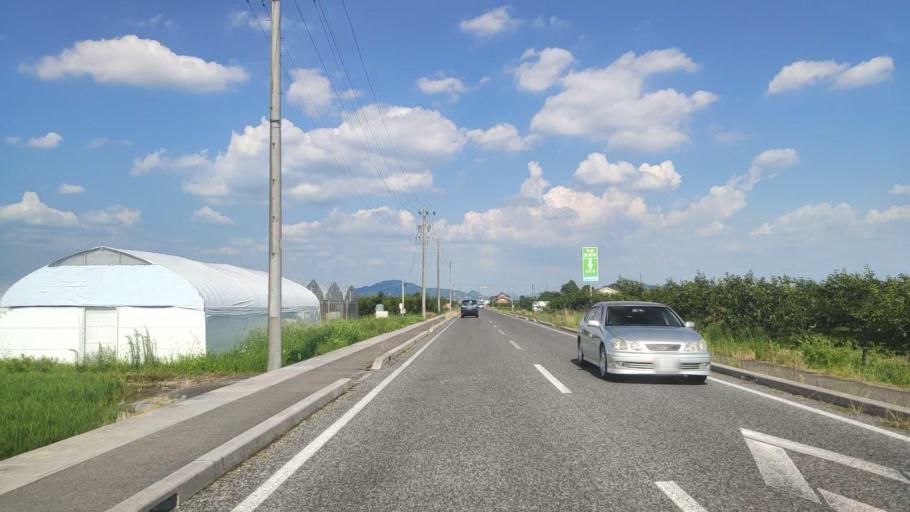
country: JP
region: Gifu
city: Gifu-shi
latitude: 35.4499
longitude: 136.6801
